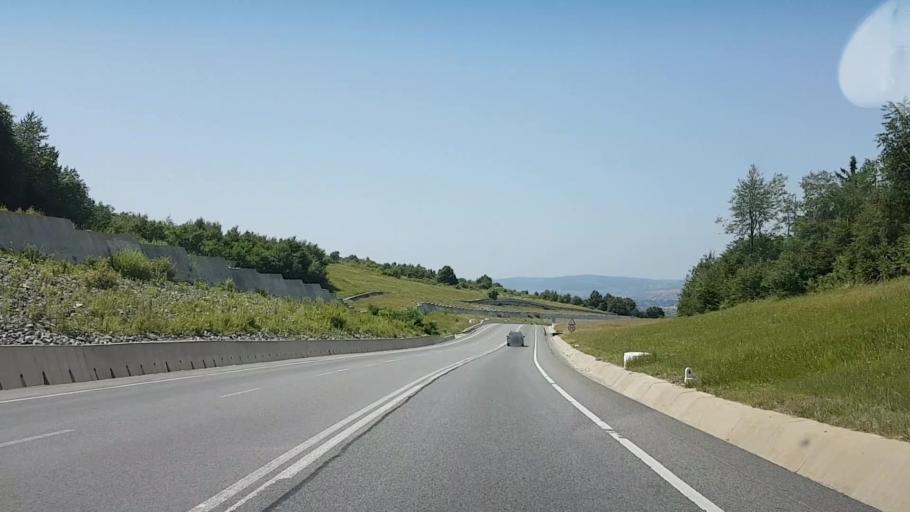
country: RO
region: Cluj
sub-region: Comuna Feleacu
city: Feleacu
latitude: 46.7207
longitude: 23.6498
